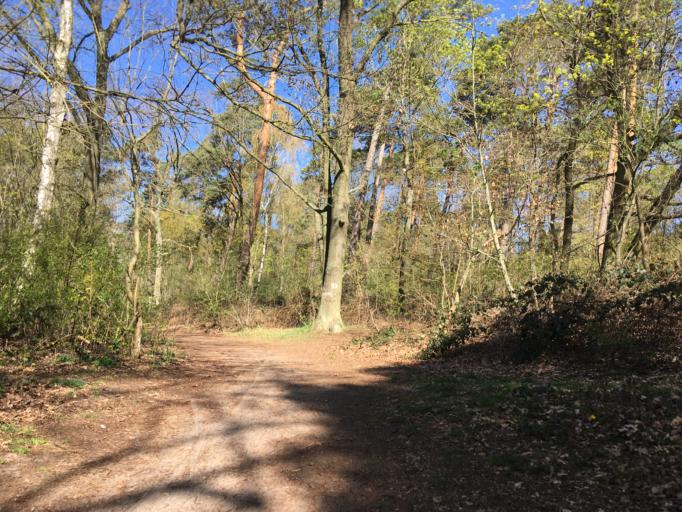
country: DE
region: Brandenburg
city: Wandlitz
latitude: 52.6881
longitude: 13.4732
